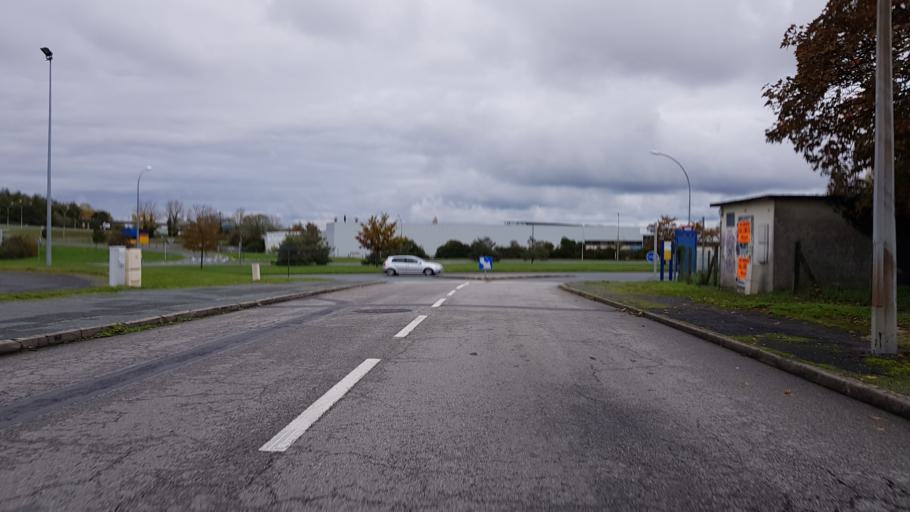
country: FR
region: Poitou-Charentes
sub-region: Departement de la Vienne
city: Chasseneuil-du-Poitou
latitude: 46.6669
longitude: 0.3748
